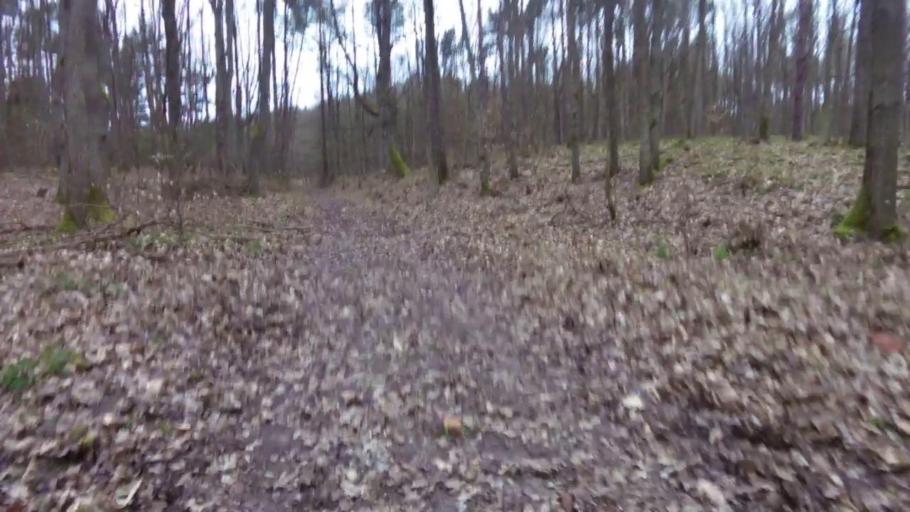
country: PL
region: West Pomeranian Voivodeship
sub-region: Powiat kamienski
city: Wolin
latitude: 53.9818
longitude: 14.6121
